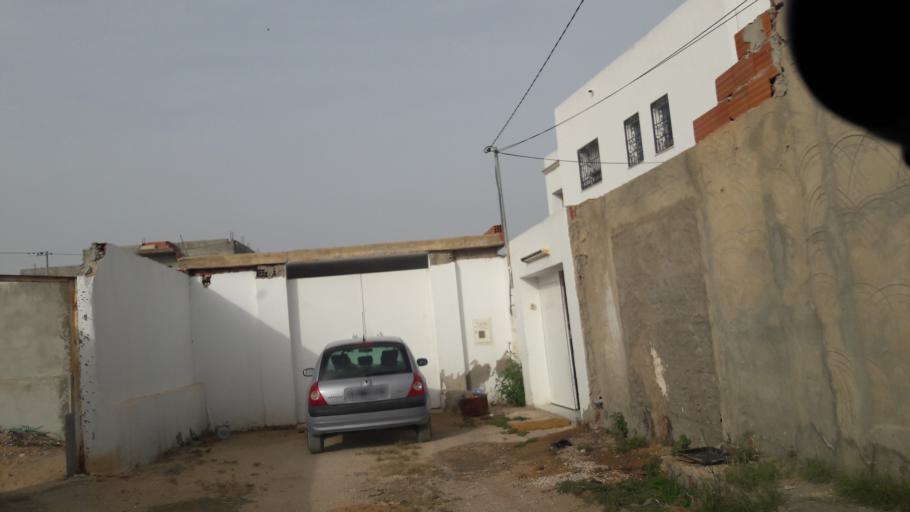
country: TN
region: Safaqis
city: Al Qarmadah
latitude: 34.7811
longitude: 10.7710
